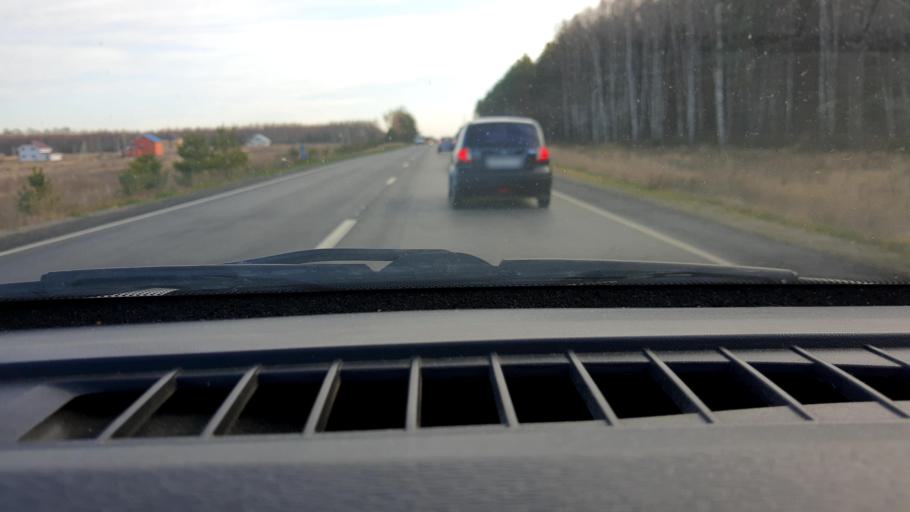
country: RU
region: Nizjnij Novgorod
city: Novaya Balakhna
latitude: 56.6086
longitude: 43.6099
